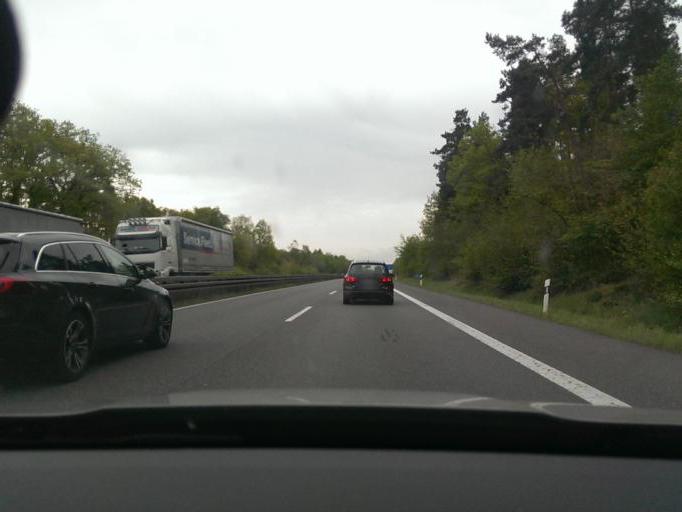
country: DE
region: Lower Saxony
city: Lehre
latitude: 52.3286
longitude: 10.7337
